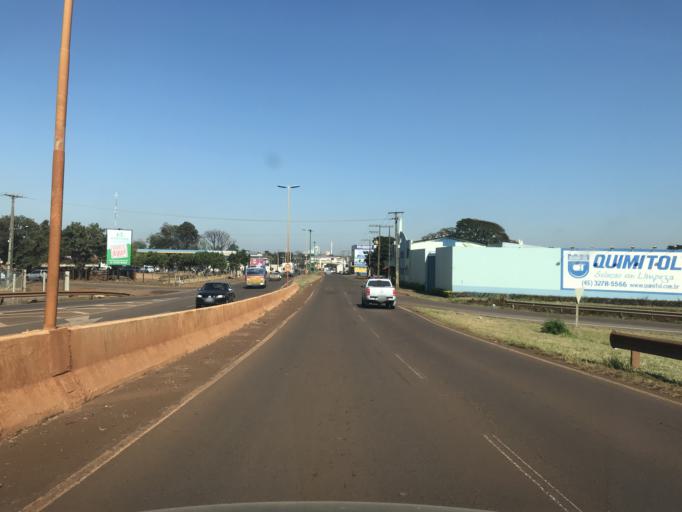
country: BR
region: Parana
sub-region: Toledo
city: Toledo
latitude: -24.7185
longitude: -53.7124
